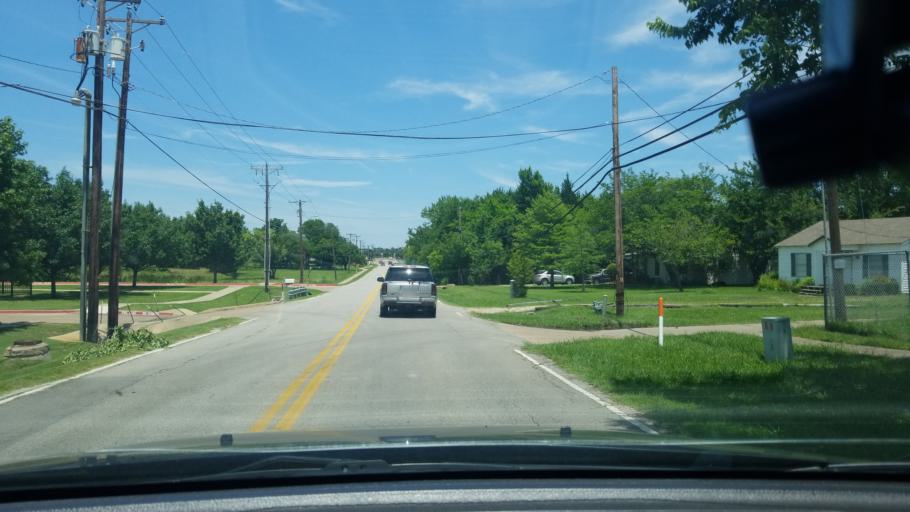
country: US
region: Texas
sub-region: Dallas County
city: Mesquite
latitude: 32.7844
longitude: -96.6010
